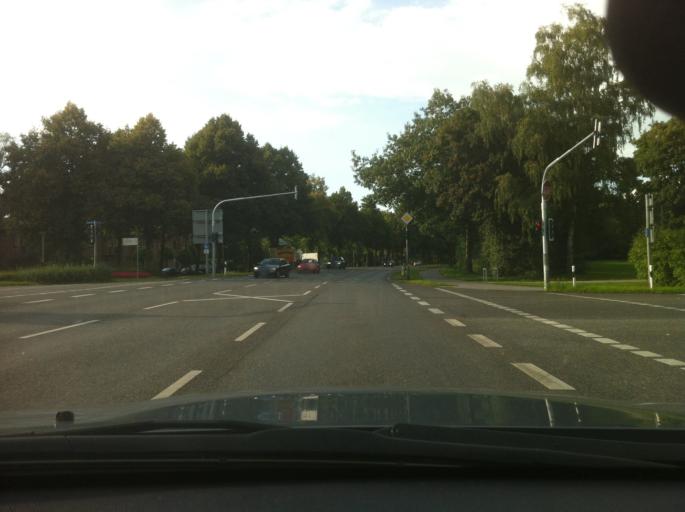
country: DE
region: North Rhine-Westphalia
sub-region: Regierungsbezirk Dusseldorf
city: Kleve
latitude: 51.7670
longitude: 6.1411
